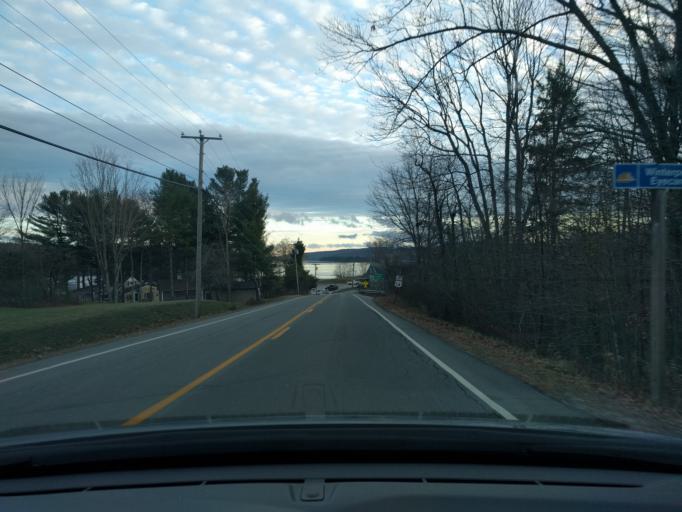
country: US
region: Maine
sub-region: Waldo County
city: Winterport
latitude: 44.6350
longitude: -68.8494
